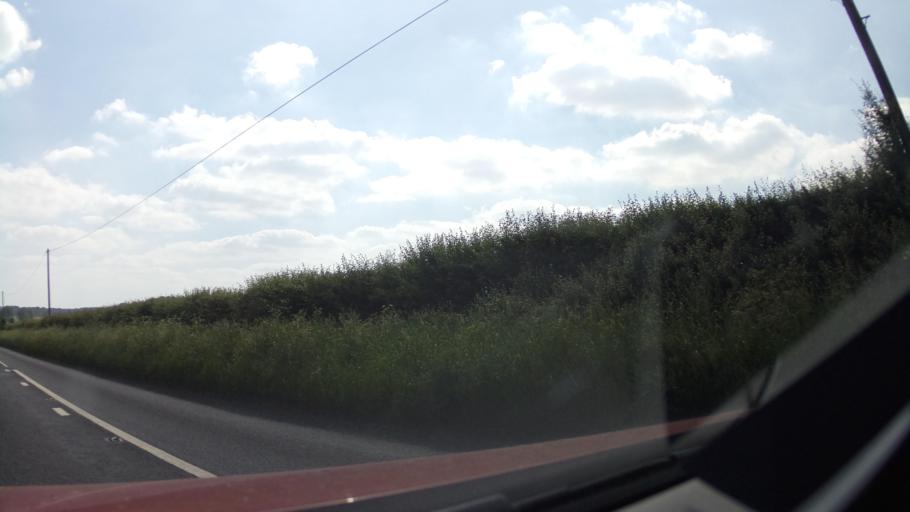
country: GB
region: England
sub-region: Wiltshire
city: Collingbourne Kingston
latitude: 51.2743
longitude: -1.6604
